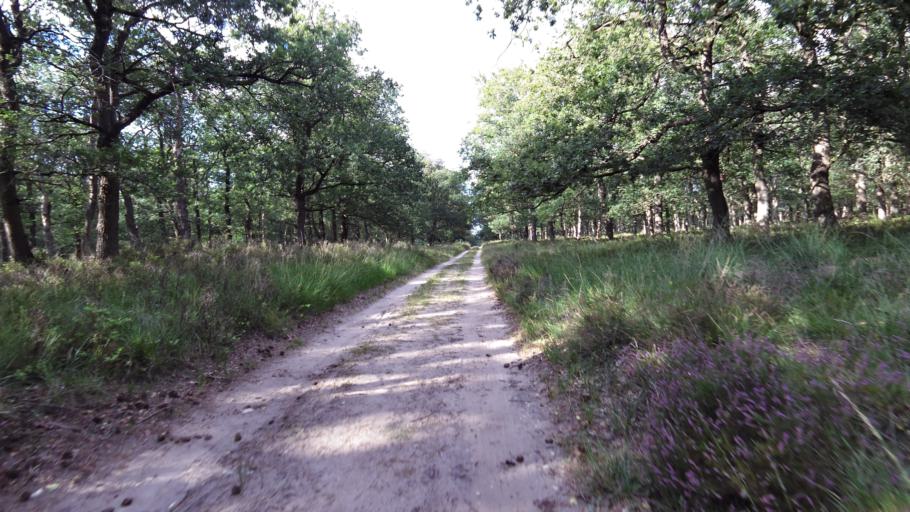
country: NL
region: Gelderland
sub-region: Gemeente Apeldoorn
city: Uddel
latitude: 52.2338
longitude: 5.8156
